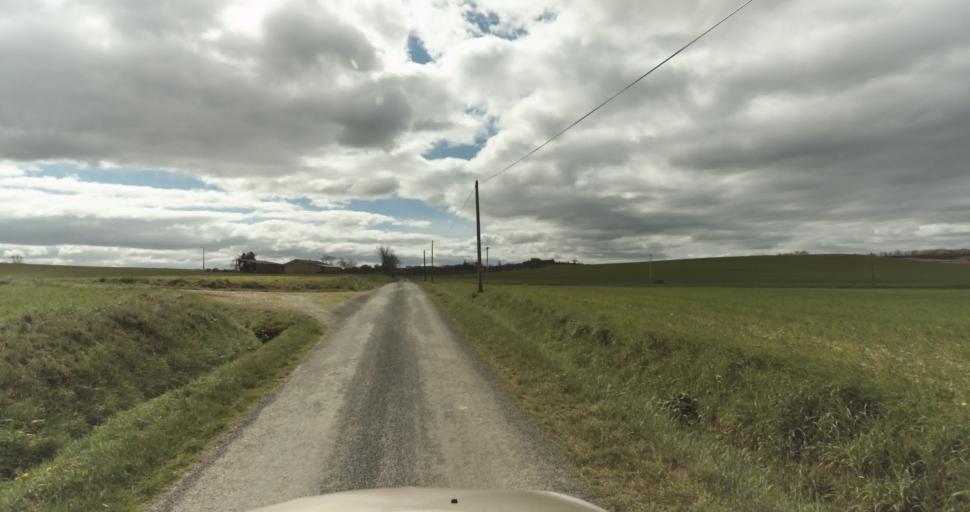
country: FR
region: Midi-Pyrenees
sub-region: Departement du Tarn
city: Puygouzon
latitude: 43.8840
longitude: 2.1779
